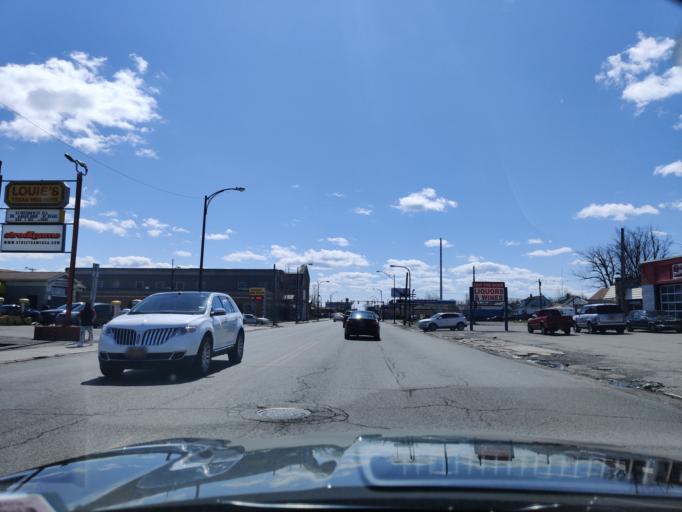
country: US
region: New York
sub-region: Erie County
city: Eggertsville
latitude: 42.9313
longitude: -78.8137
